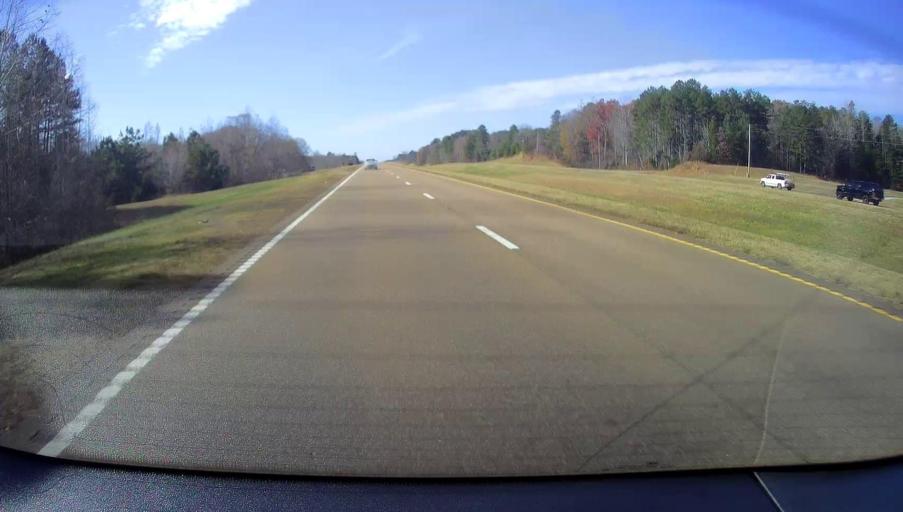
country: US
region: Mississippi
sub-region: Benton County
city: Ashland
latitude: 34.9514
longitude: -89.0669
